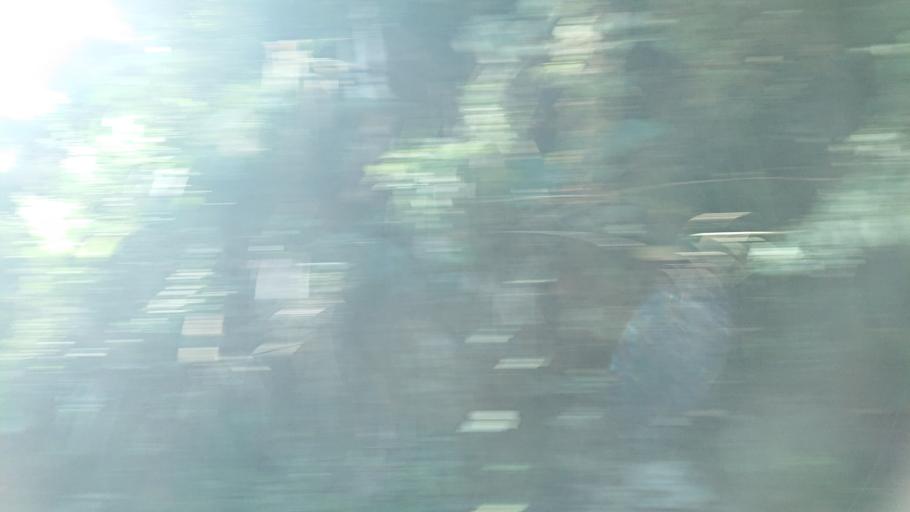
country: TW
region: Taiwan
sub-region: Chiayi
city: Jiayi Shi
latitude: 23.5359
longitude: 120.6357
